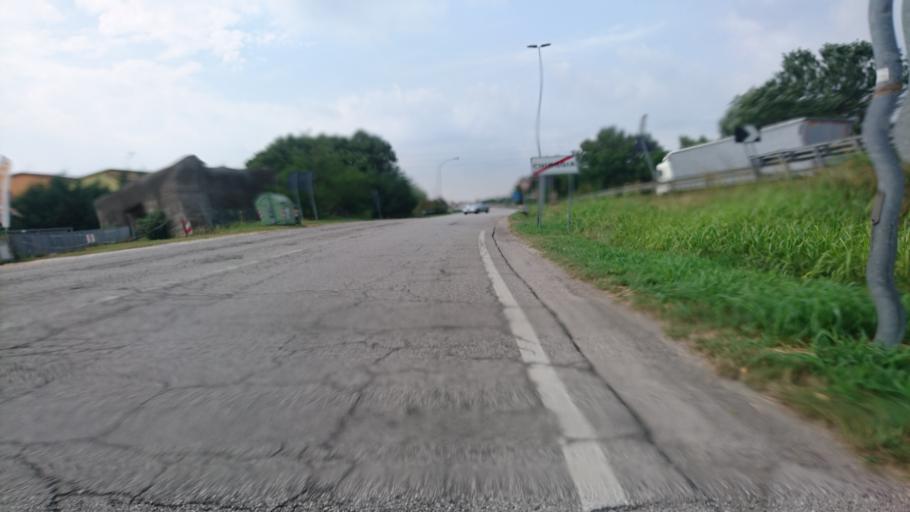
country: IT
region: Veneto
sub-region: Provincia di Venezia
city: Sant'Anna
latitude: 45.1817
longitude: 12.2782
